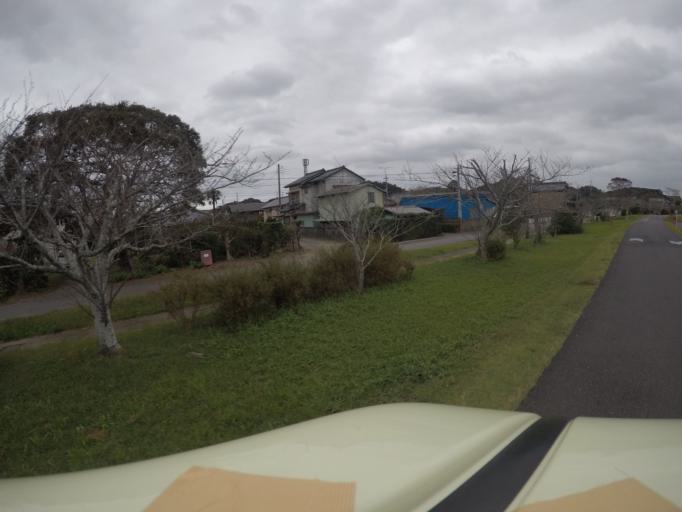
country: JP
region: Ibaraki
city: Itako
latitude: 35.9797
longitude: 140.4958
